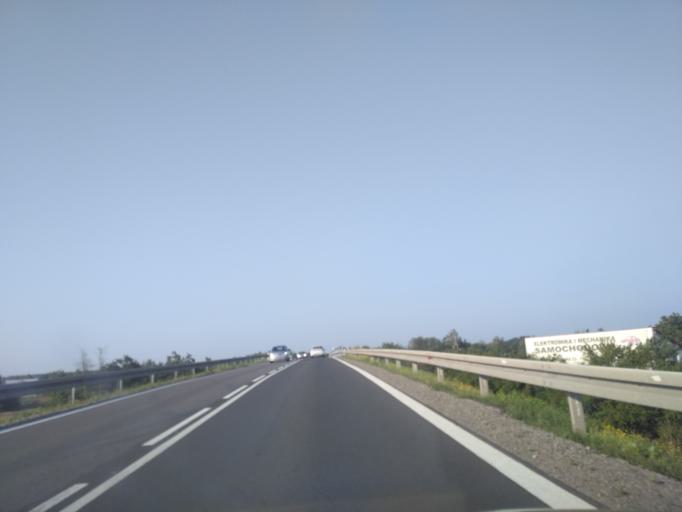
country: PL
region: Subcarpathian Voivodeship
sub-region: Powiat nizanski
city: Nisko
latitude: 50.5116
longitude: 22.1490
